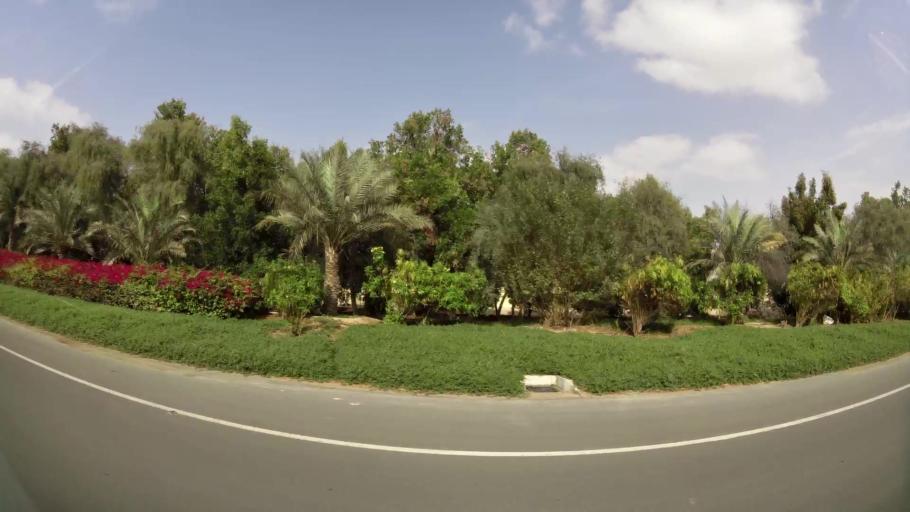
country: AE
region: Abu Dhabi
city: Abu Dhabi
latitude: 24.3994
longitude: 54.5310
